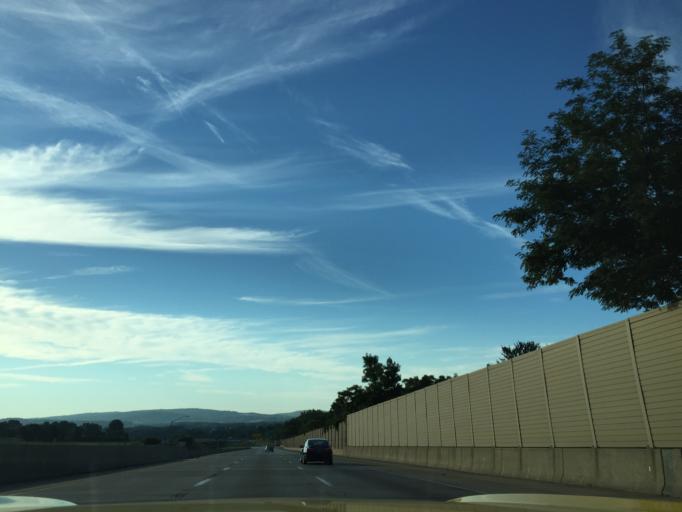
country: US
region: Pennsylvania
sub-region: Lehigh County
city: Emmaus
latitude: 40.5574
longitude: -75.4405
